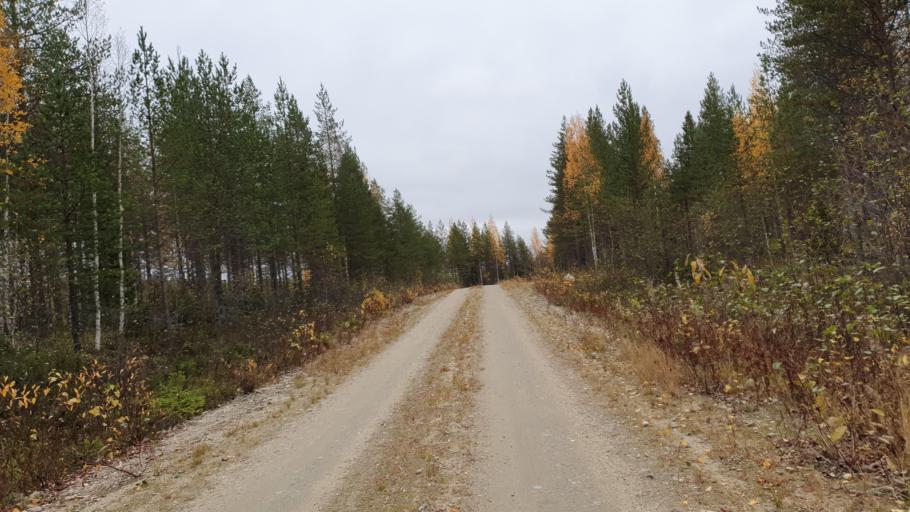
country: FI
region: Kainuu
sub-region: Kehys-Kainuu
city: Kuhmo
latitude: 64.4446
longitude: 29.6124
